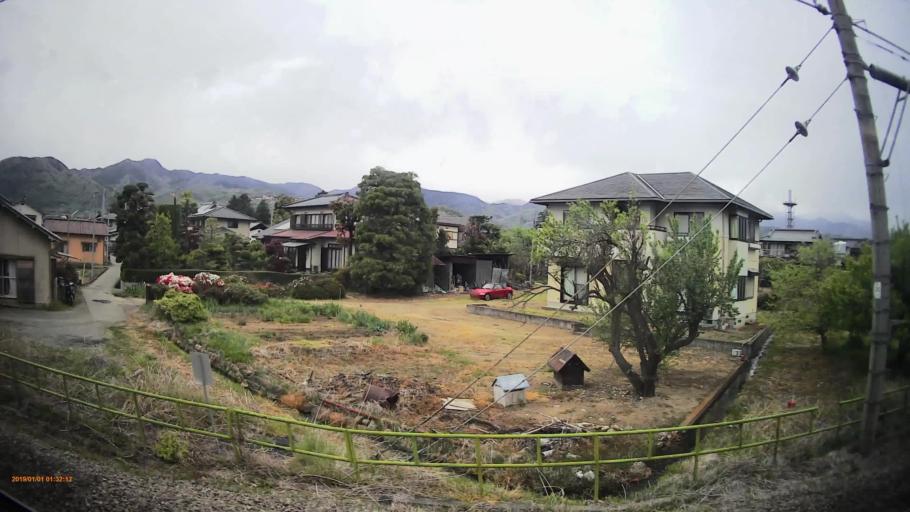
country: JP
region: Yamanashi
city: Enzan
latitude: 35.6869
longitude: 138.6897
